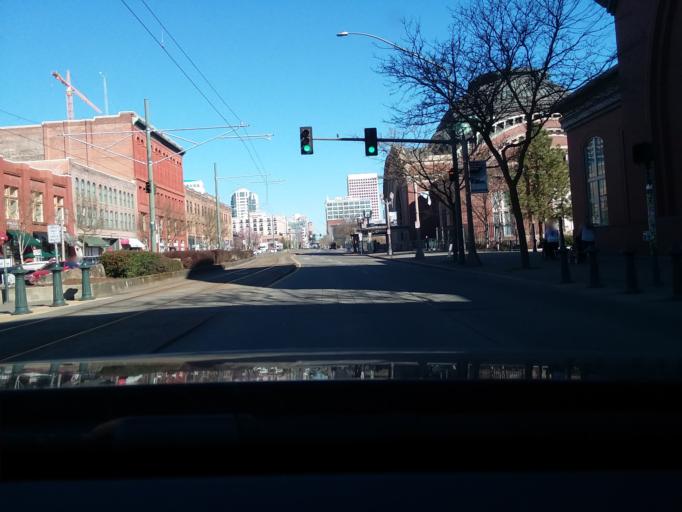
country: US
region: Washington
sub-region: Pierce County
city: Tacoma
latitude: 47.2450
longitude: -122.4366
